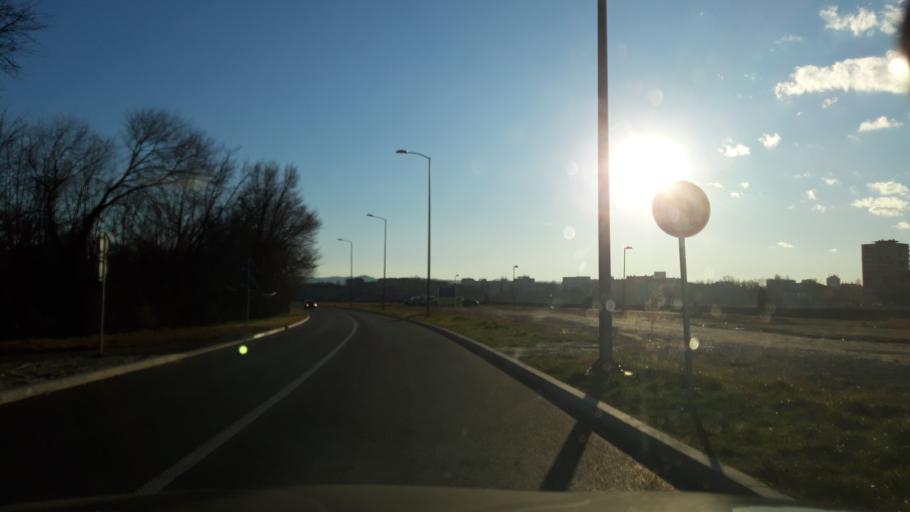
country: RS
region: Autonomna Pokrajina Vojvodina
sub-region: Juznobacki Okrug
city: Petrovaradin
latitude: 45.2590
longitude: 19.8602
